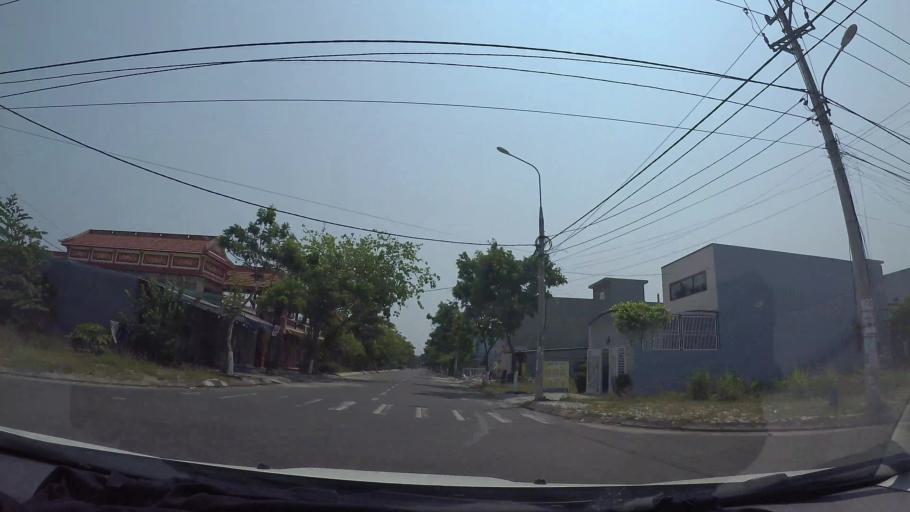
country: VN
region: Da Nang
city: Cam Le
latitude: 15.9993
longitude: 108.2046
